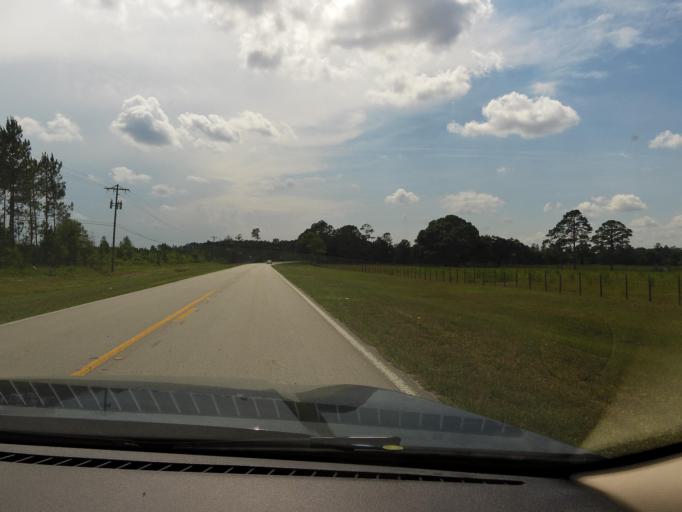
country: US
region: Florida
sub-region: Baker County
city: Macclenny
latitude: 30.2012
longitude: -82.0461
